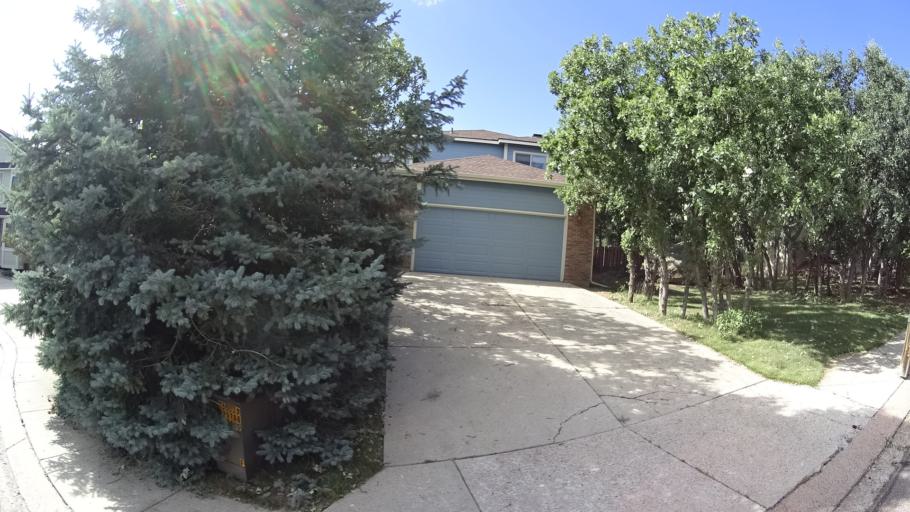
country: US
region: Colorado
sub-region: El Paso County
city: Fort Carson
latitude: 38.7612
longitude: -104.8311
